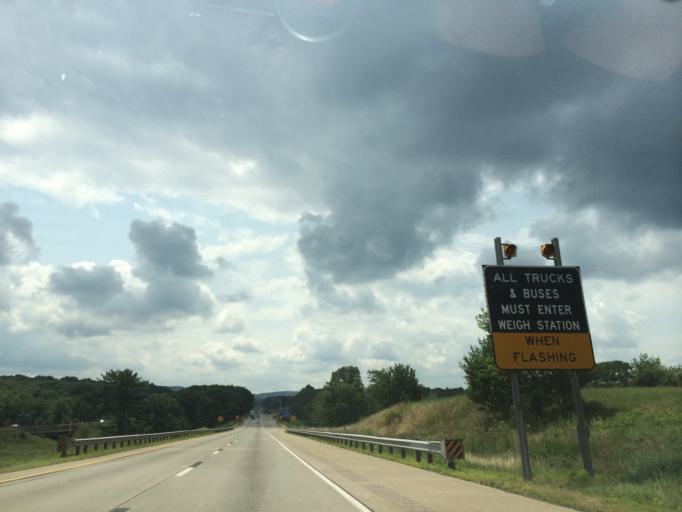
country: US
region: Pennsylvania
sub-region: Luzerne County
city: Nanticoke
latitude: 41.1367
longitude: -75.9634
